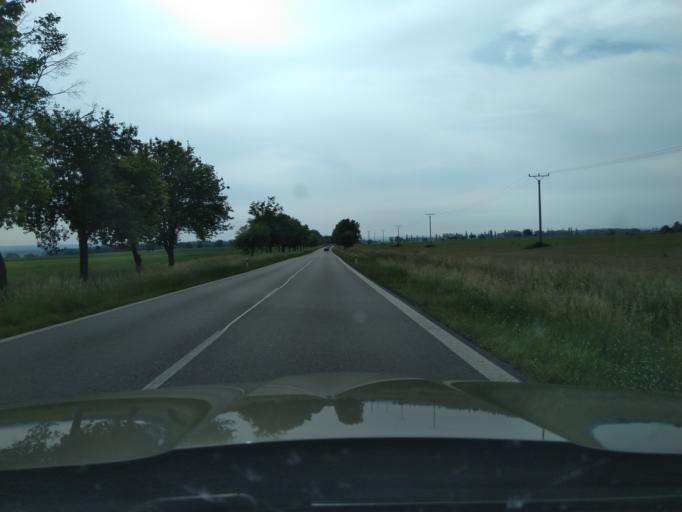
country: CZ
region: Jihocesky
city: Netolice
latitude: 49.0334
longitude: 14.2534
